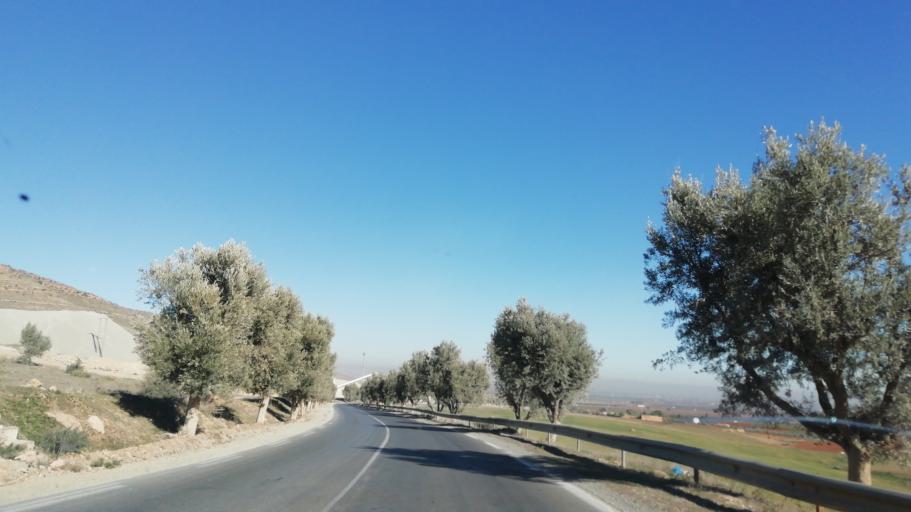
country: DZ
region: Mascara
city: Mascara
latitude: 35.2493
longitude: 0.1215
